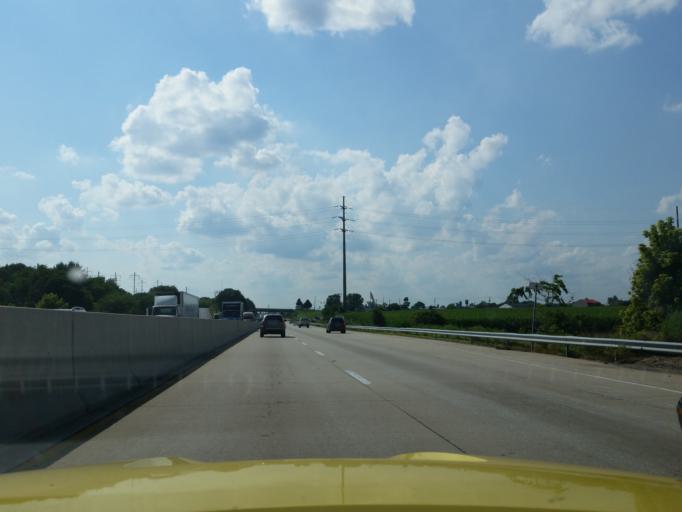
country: US
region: Pennsylvania
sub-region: Lancaster County
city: East Petersburg
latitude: 40.0865
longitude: -76.3756
